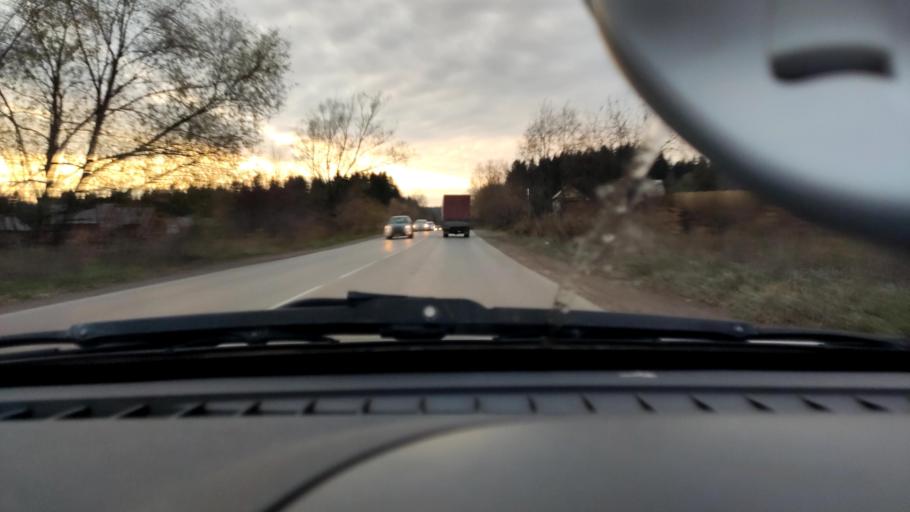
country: RU
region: Perm
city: Ferma
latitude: 57.9573
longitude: 56.3688
